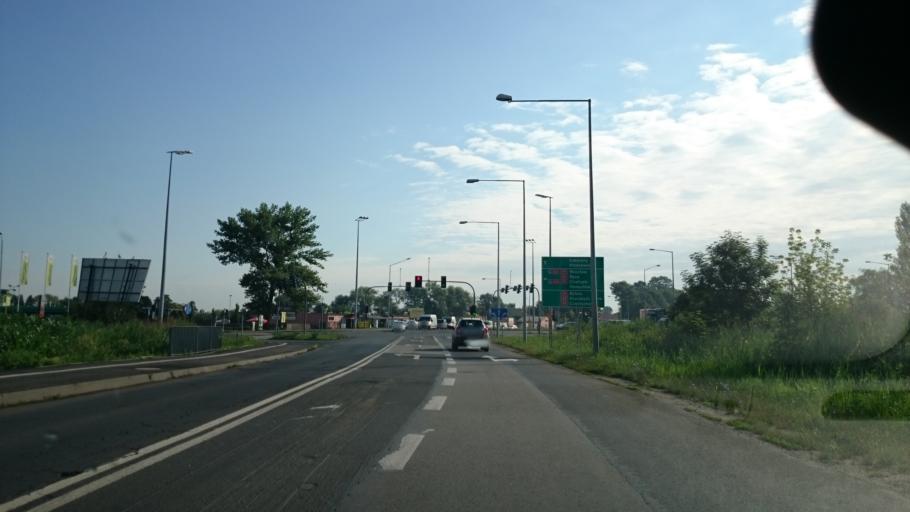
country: PL
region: Opole Voivodeship
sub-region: Powiat opolski
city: Opole
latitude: 50.7030
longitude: 17.9335
